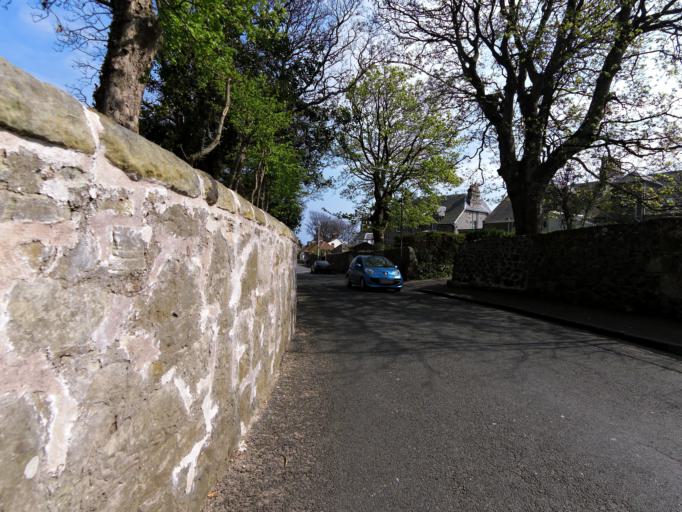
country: GB
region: Scotland
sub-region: Fife
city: Kinghorn
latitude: 56.0725
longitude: -3.1790
